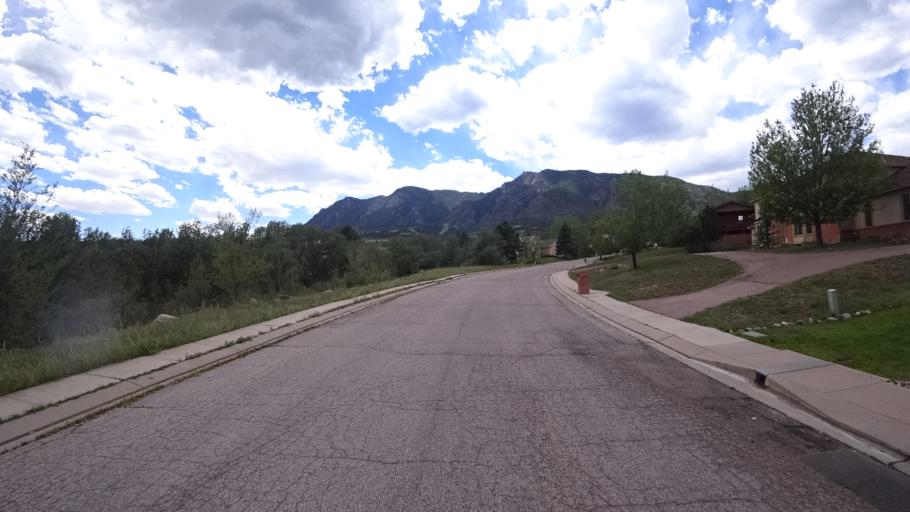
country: US
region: Colorado
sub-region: El Paso County
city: Stratmoor
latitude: 38.7786
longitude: -104.8341
